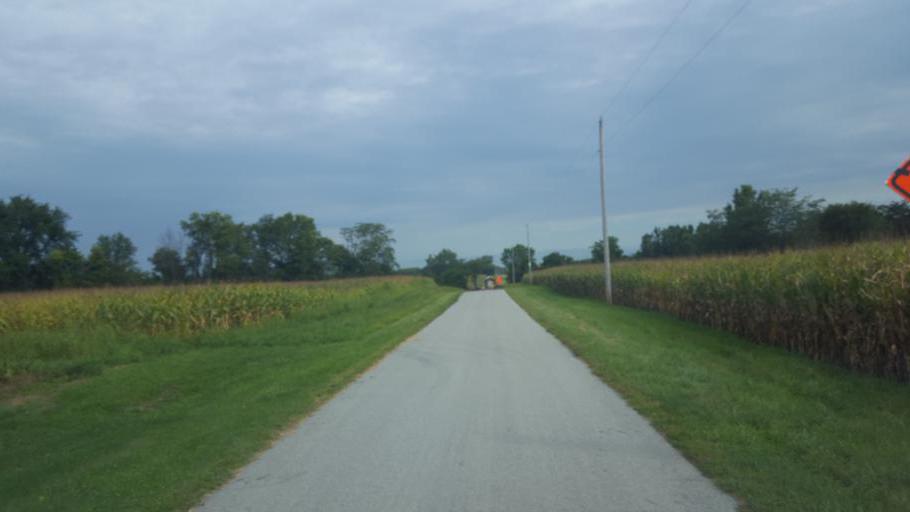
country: US
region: Ohio
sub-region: Wyandot County
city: Upper Sandusky
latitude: 40.7675
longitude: -83.1690
